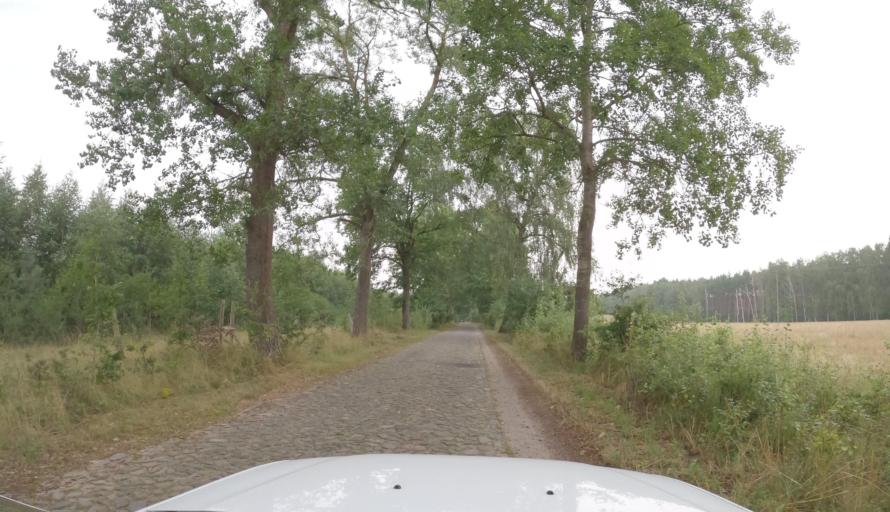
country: PL
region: West Pomeranian Voivodeship
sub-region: Powiat kolobrzeski
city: Ryman
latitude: 53.8531
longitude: 15.5854
